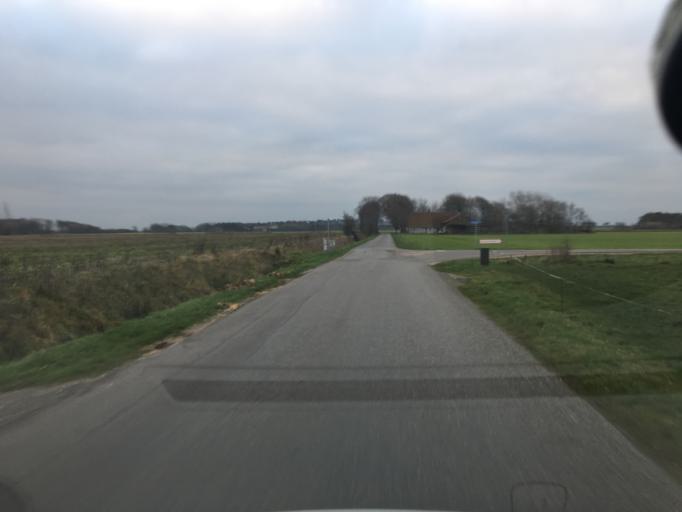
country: DK
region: South Denmark
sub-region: Tonder Kommune
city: Logumkloster
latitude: 55.0618
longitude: 9.0667
